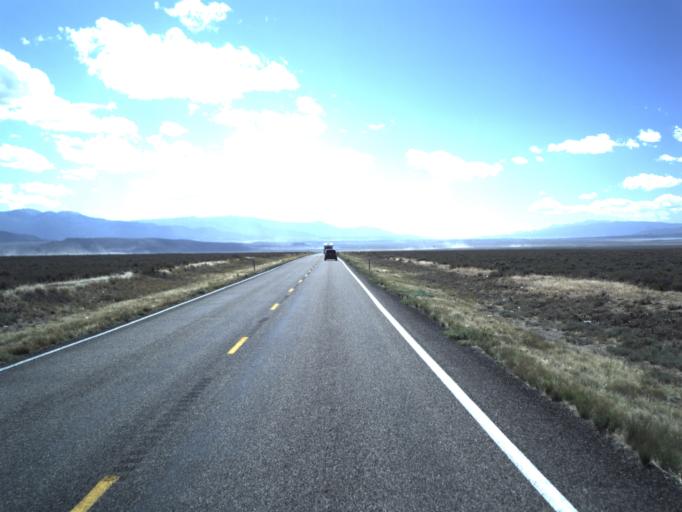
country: US
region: Utah
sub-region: Iron County
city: Enoch
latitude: 37.9803
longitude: -113.0036
